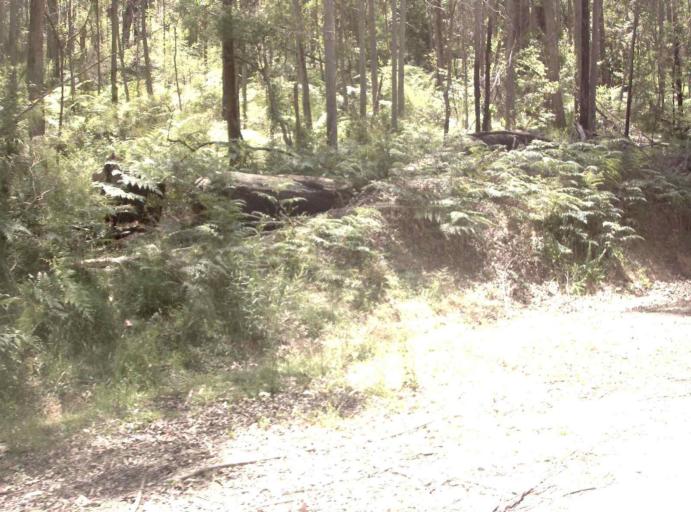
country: AU
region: New South Wales
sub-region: Bombala
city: Bombala
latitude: -37.5099
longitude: 148.9278
